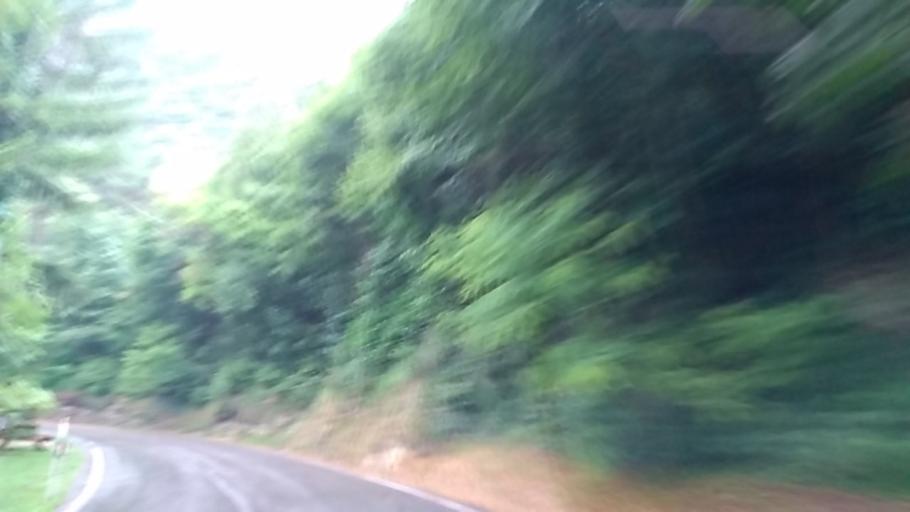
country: IT
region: Lombardy
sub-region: Provincia di Brescia
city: Pieve
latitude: 45.7905
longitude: 10.7397
